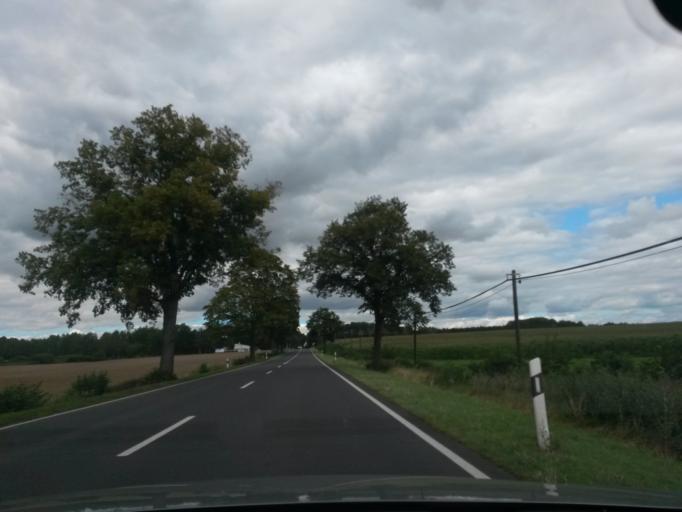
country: DE
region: Brandenburg
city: Angermunde
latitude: 52.9868
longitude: 13.9780
